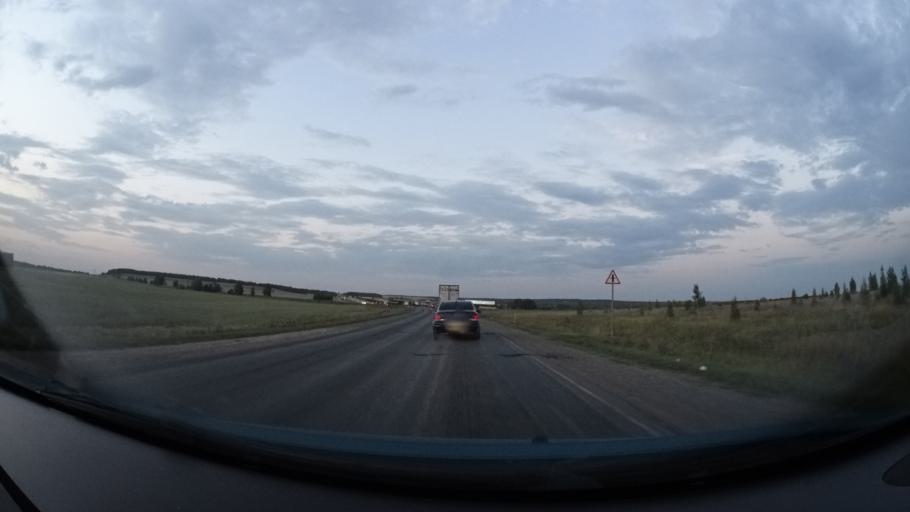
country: RU
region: Tatarstan
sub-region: Bavlinskiy Rayon
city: Bavly
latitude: 54.2714
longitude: 52.9779
